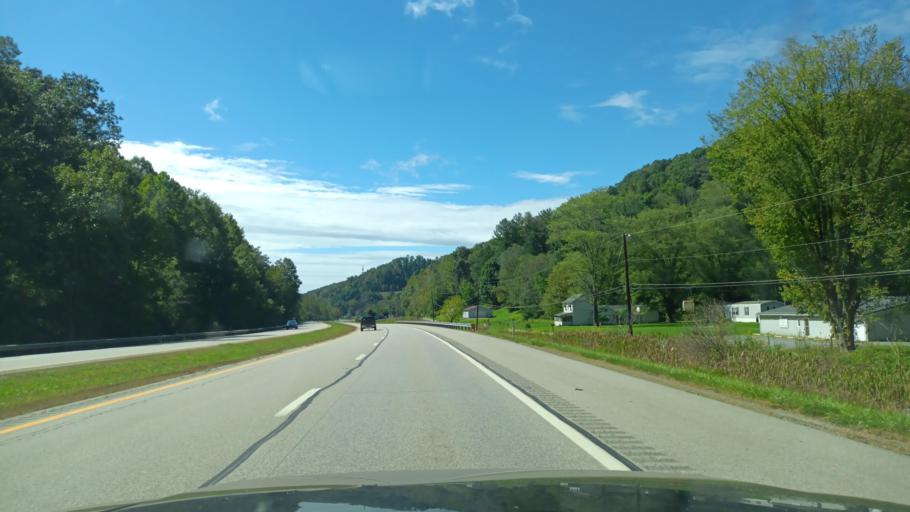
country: US
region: West Virginia
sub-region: Harrison County
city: Salem
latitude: 39.2964
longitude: -80.6222
